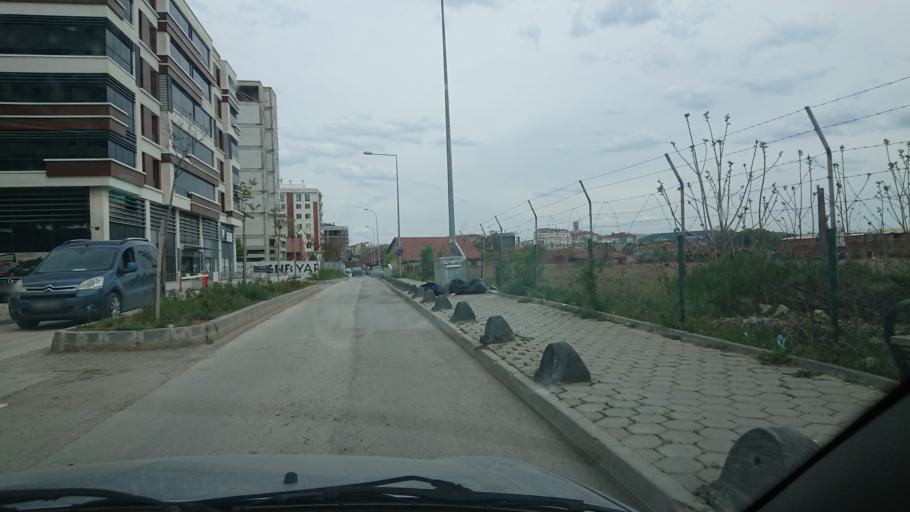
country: TR
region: Eskisehir
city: Eskisehir
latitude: 39.7827
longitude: 30.5047
